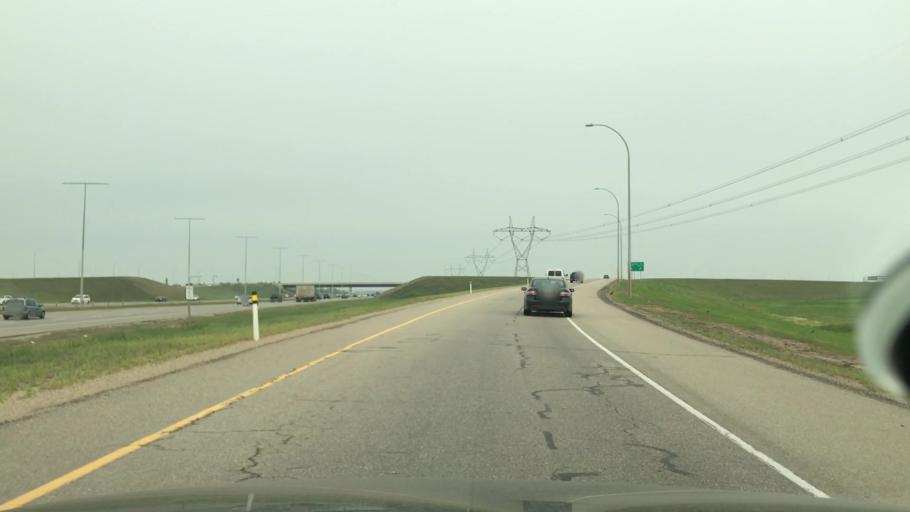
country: CA
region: Alberta
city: Devon
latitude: 53.4394
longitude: -113.5961
